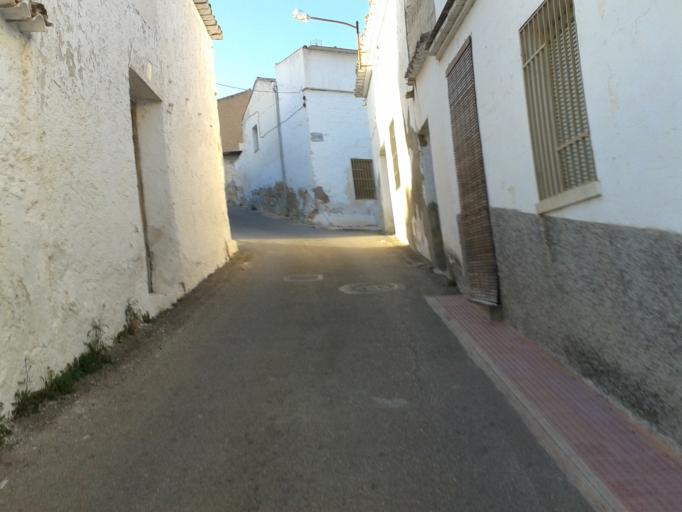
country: ES
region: Castille-La Mancha
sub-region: Provincia de Albacete
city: Caudete
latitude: 38.7044
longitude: -0.9907
